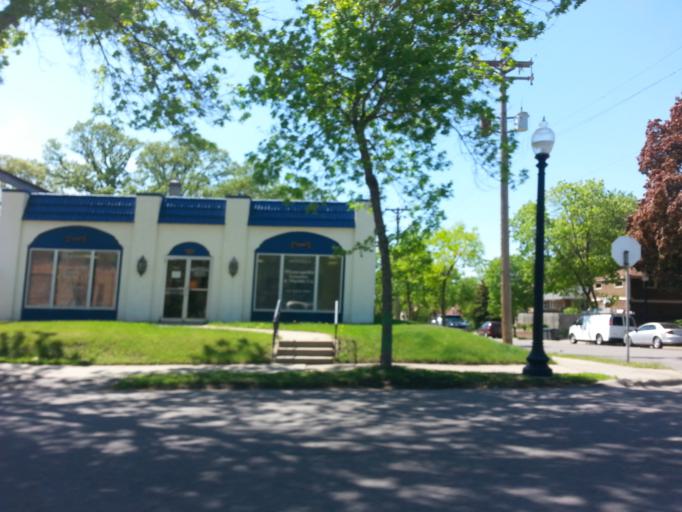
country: US
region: Minnesota
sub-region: Hennepin County
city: Richfield
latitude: 44.9231
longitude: -93.2625
